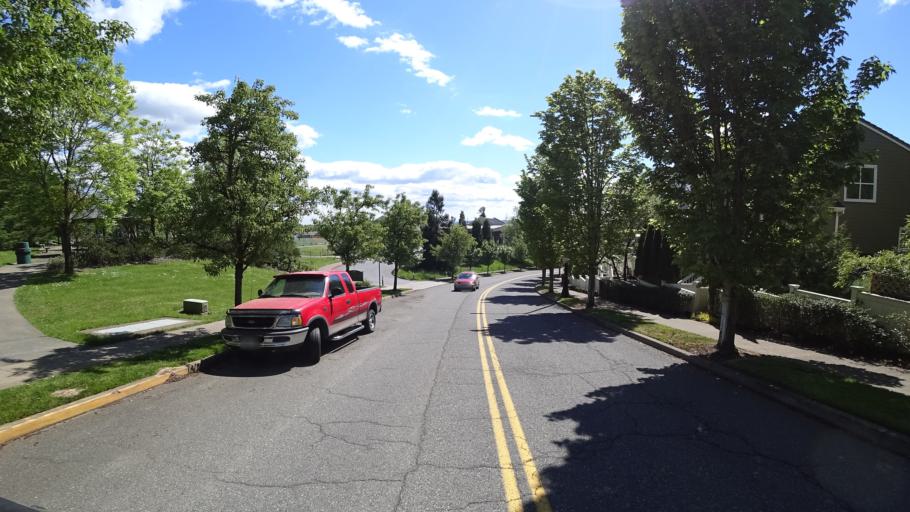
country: US
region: Oregon
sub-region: Washington County
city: West Haven
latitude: 45.5439
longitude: -122.7769
